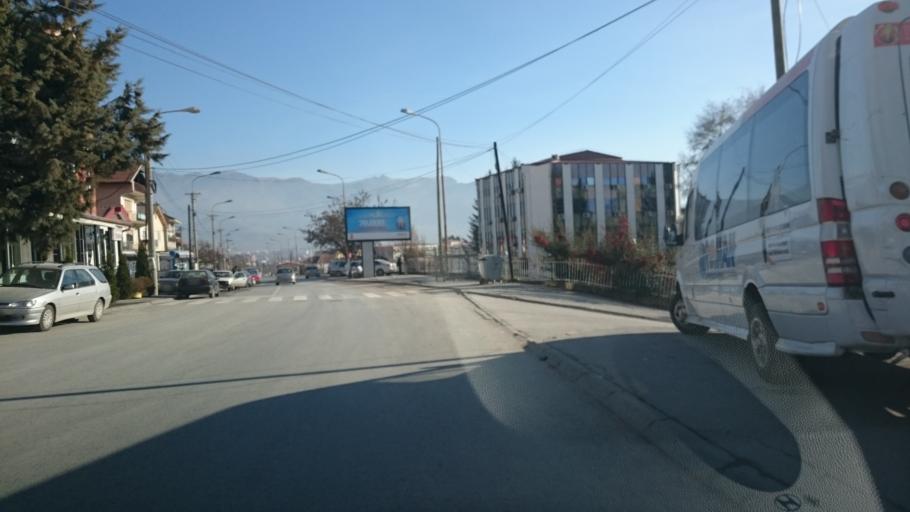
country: MK
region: Prilep
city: Markov Grad
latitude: 41.3548
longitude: 21.5405
